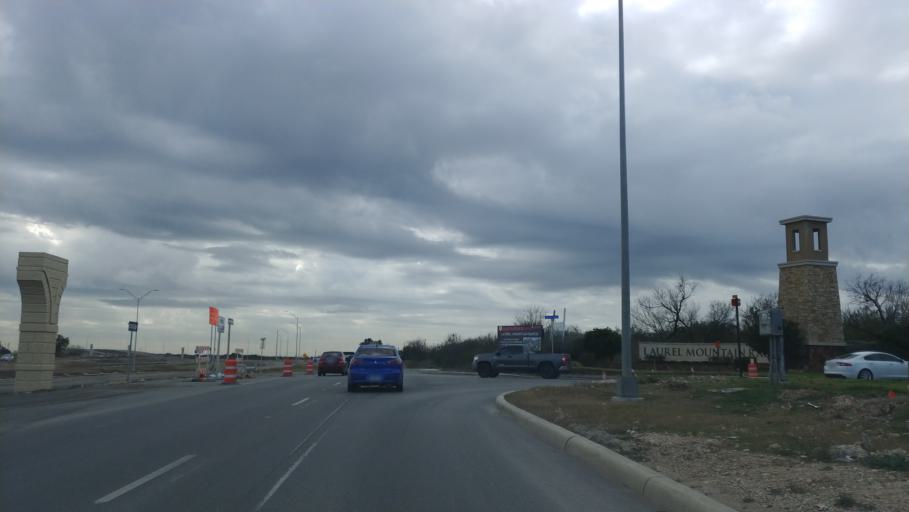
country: US
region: Texas
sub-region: Bexar County
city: Lackland Air Force Base
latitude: 29.4113
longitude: -98.7103
